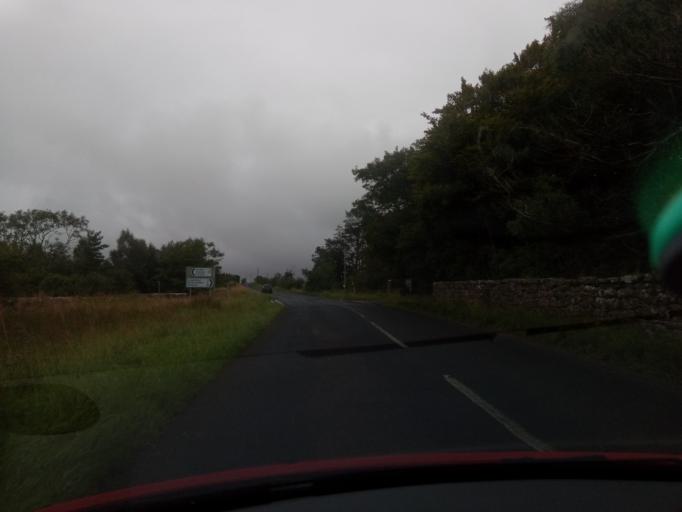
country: GB
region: England
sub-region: Northumberland
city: Rothley
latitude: 55.2008
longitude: -1.9331
